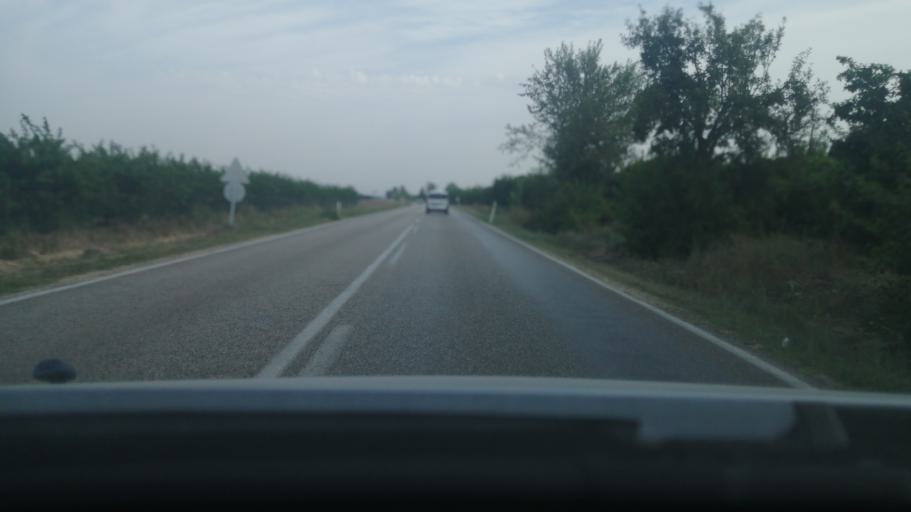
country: TR
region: Adana
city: Kozan
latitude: 37.3674
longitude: 35.8532
